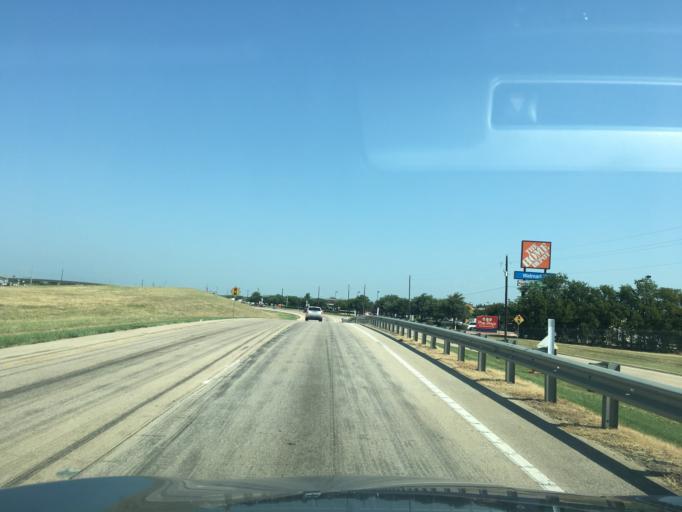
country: US
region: Texas
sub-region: Denton County
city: Roanoke
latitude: 33.0086
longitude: -97.2192
